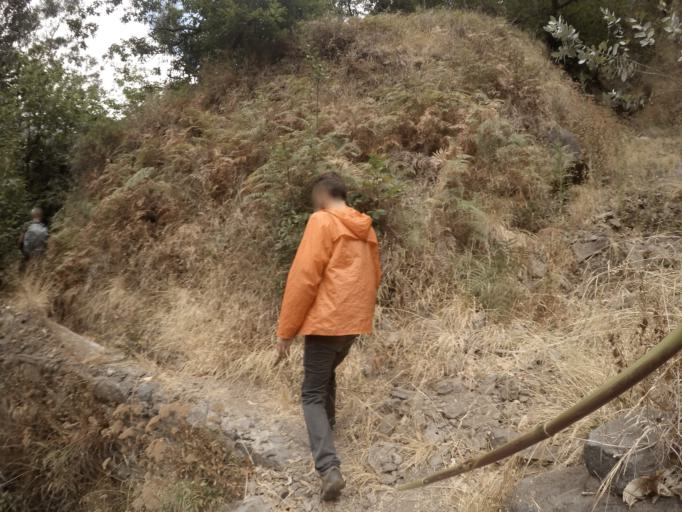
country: PT
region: Madeira
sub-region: Camara de Lobos
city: Curral das Freiras
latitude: 32.7084
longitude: -16.9684
